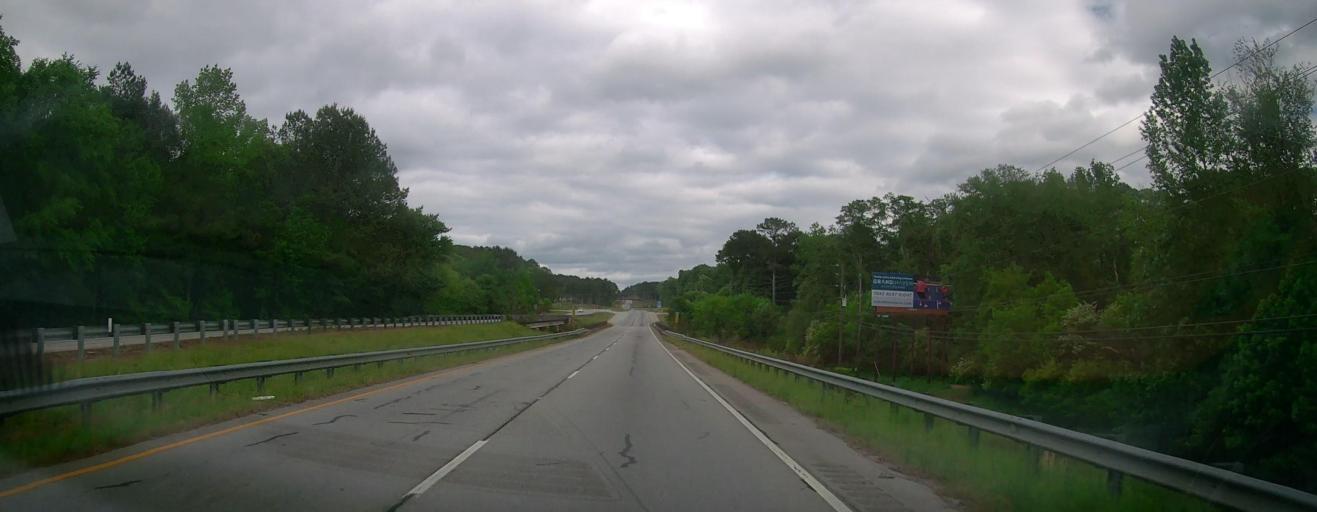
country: US
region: Georgia
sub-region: Walton County
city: Monroe
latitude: 33.8050
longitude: -83.7608
